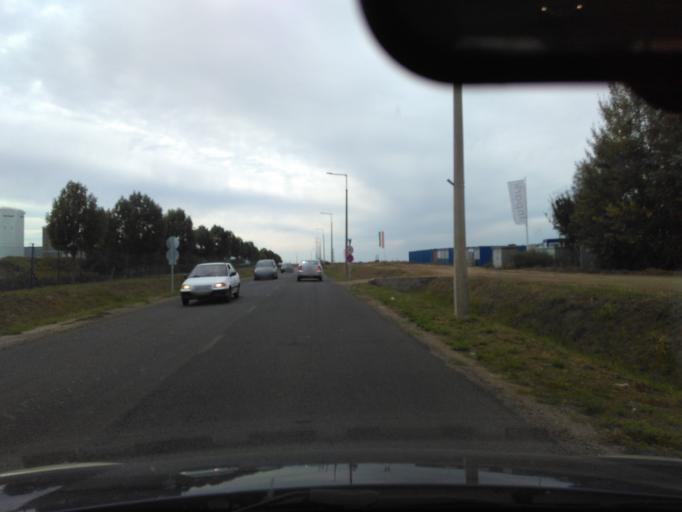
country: HU
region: Heves
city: Hatvan
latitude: 47.6699
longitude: 19.6456
